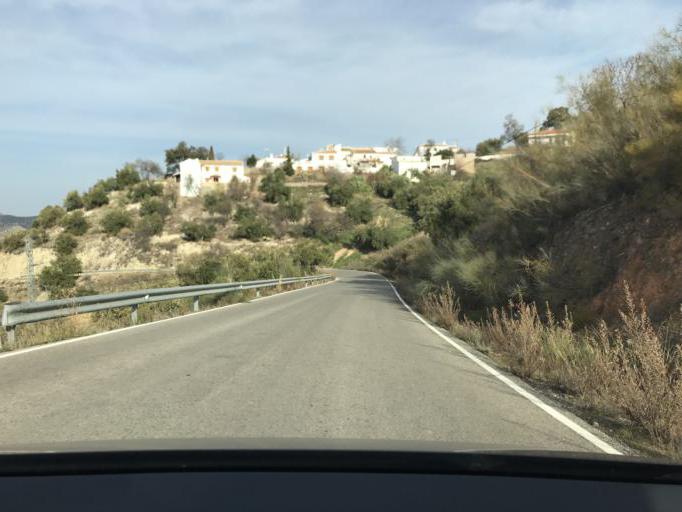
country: ES
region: Andalusia
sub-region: Provincia de Granada
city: Algarinejo
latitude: 37.3193
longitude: -4.1459
